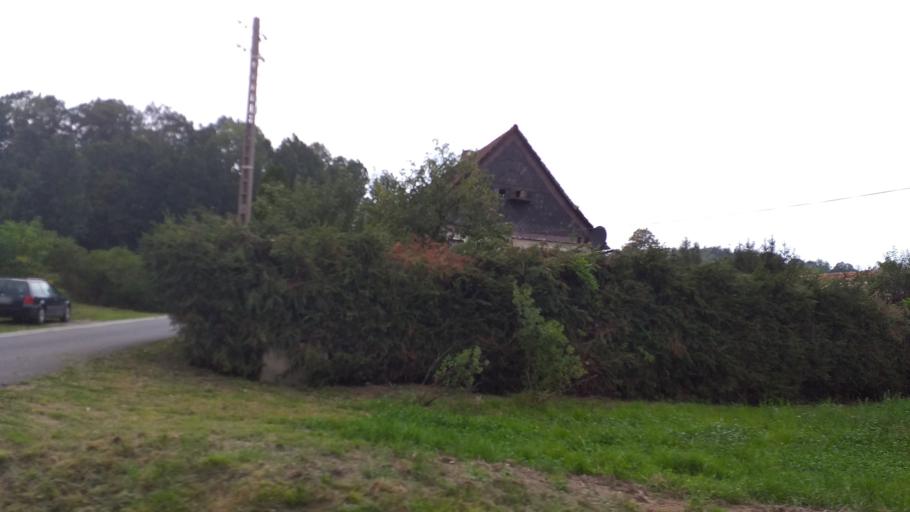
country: PL
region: Lower Silesian Voivodeship
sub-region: Powiat lubanski
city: Lesna
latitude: 51.0542
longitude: 15.2726
